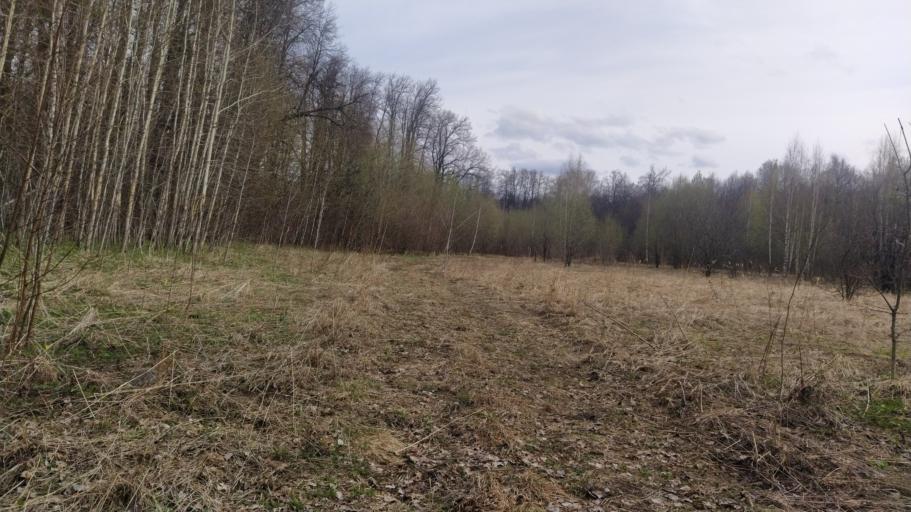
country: RU
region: Chuvashia
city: Novyye Lapsary
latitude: 56.1404
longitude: 47.1230
